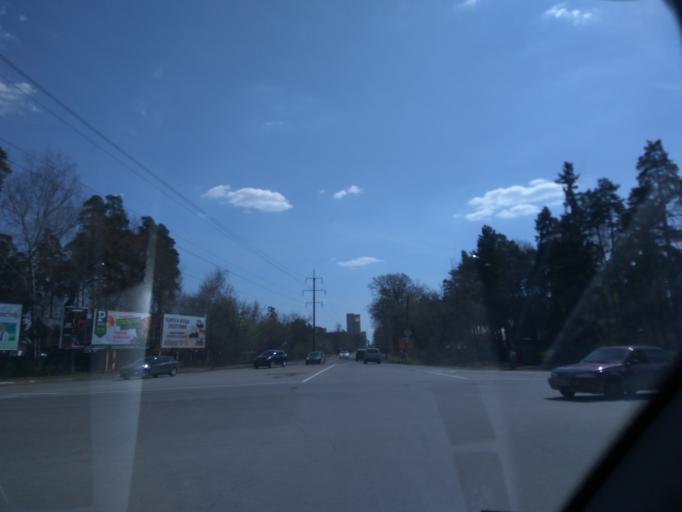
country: RU
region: Moskovskaya
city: Kratovo
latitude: 55.5723
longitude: 38.1844
